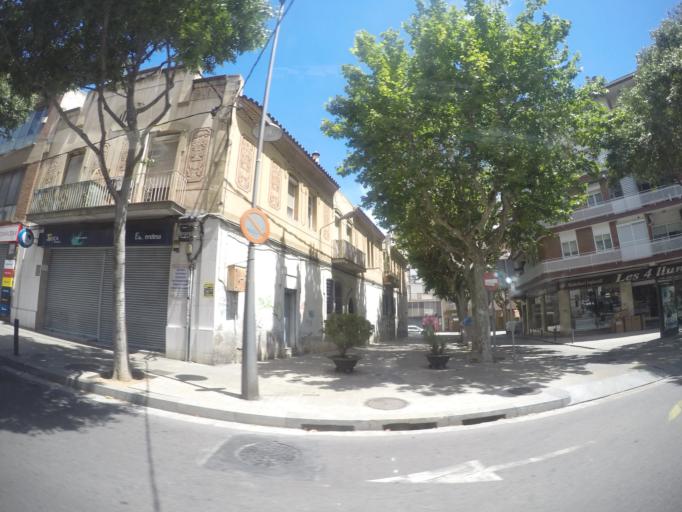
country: ES
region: Catalonia
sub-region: Provincia de Barcelona
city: Badalona
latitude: 41.4538
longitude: 2.2482
